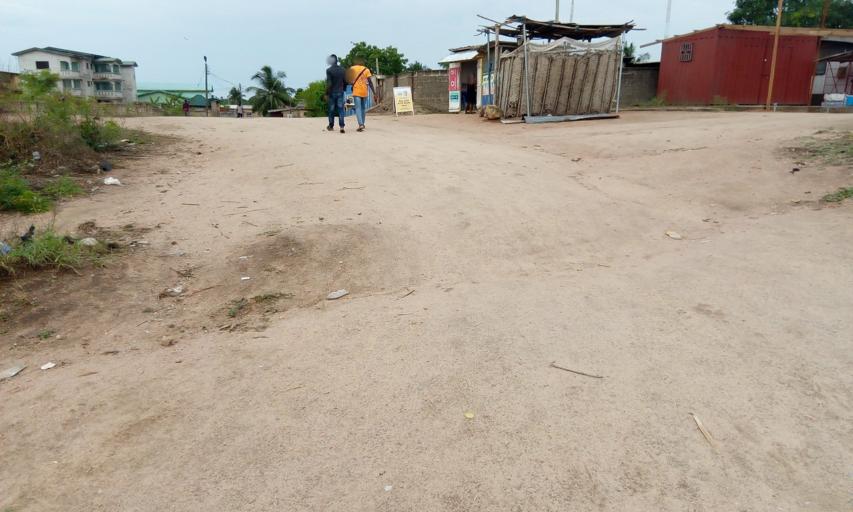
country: GH
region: Central
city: Winneba
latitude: 5.3579
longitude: -0.6204
